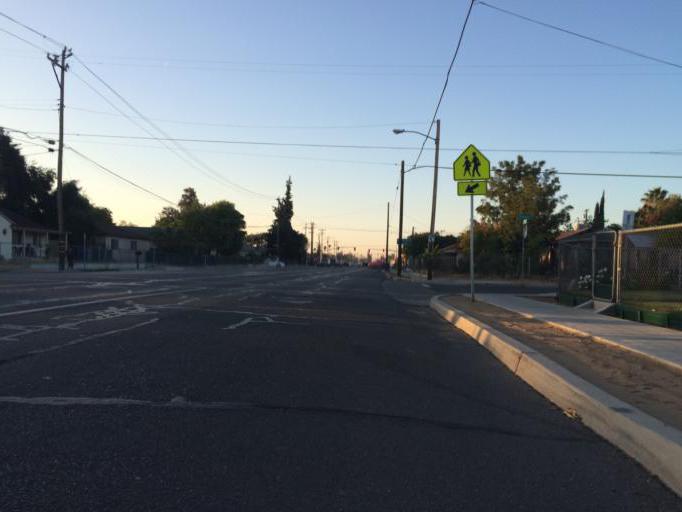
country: US
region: California
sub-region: Fresno County
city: Fresno
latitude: 36.7598
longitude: -119.7546
